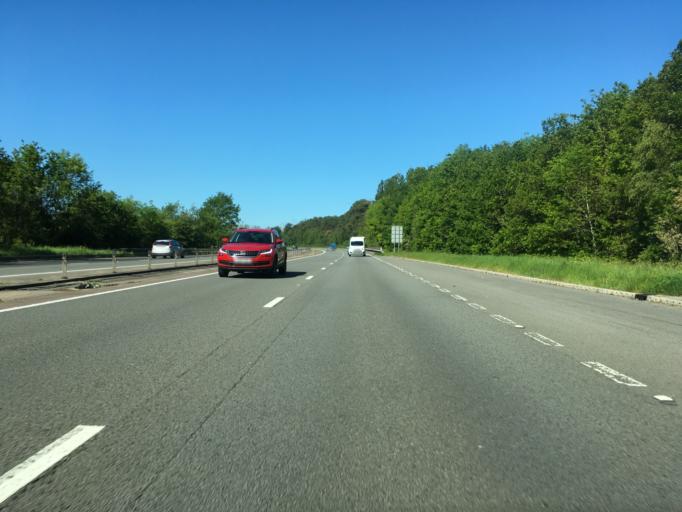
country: GB
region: Wales
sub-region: Monmouthshire
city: Mitchel Troy
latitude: 51.7851
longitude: -2.7818
